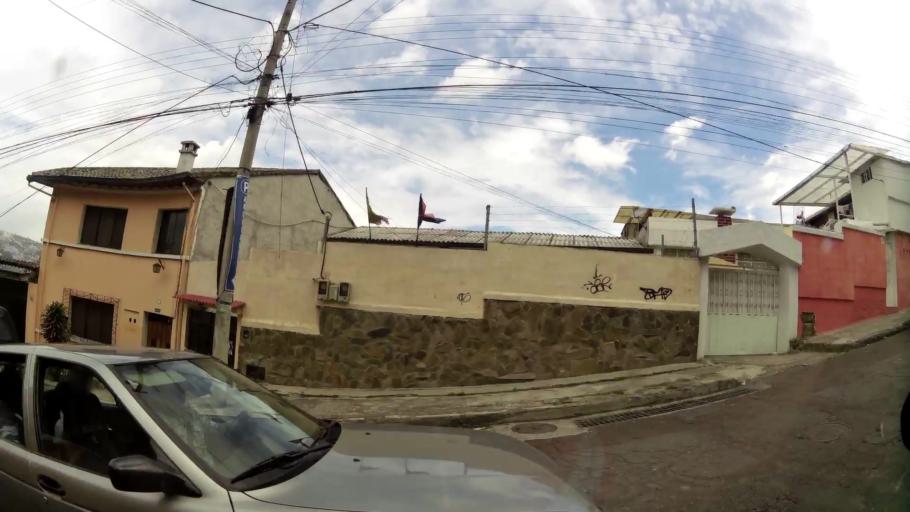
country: EC
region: Pichincha
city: Quito
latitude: -0.2147
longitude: -78.5141
